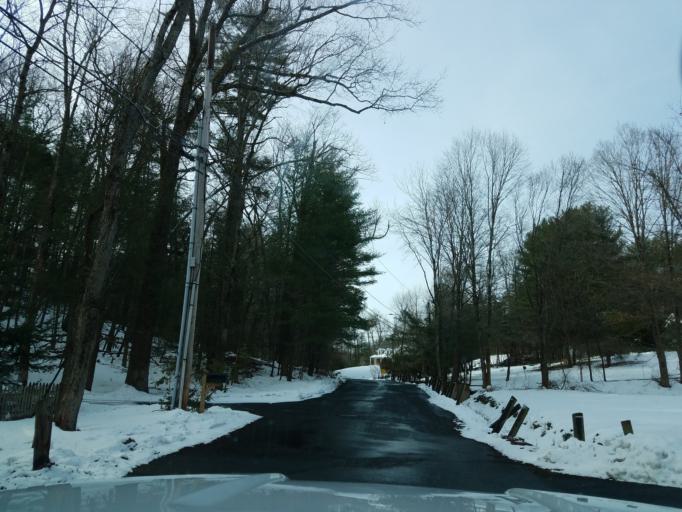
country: US
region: Connecticut
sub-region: Hartford County
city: Weatogue
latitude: 41.7966
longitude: -72.8187
